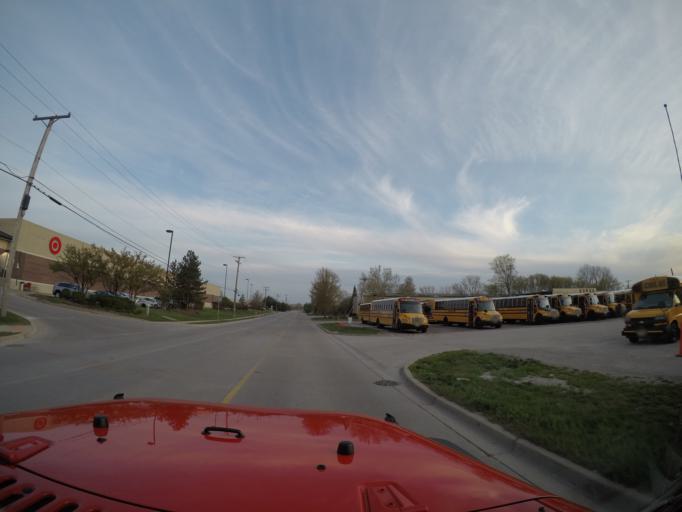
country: US
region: Illinois
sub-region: Cook County
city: Northbrook
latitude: 42.1028
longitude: -87.8149
